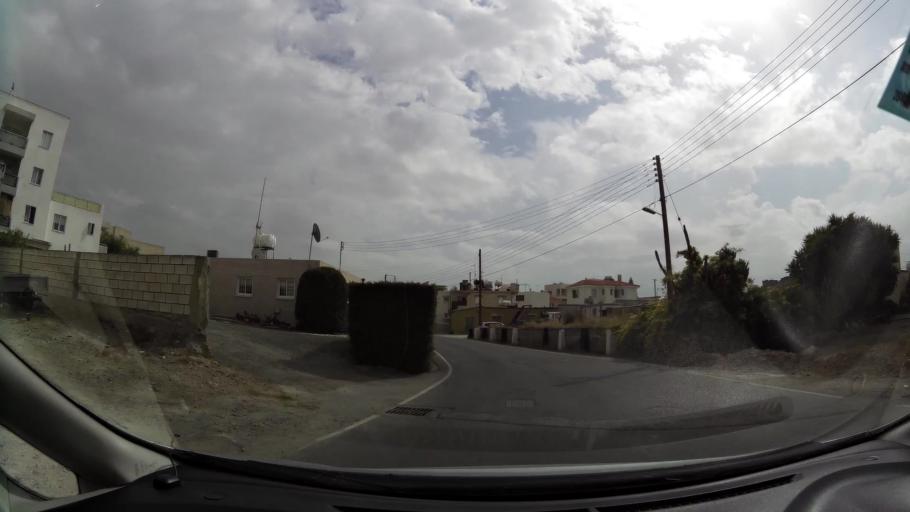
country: CY
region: Lefkosia
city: Geri
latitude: 35.1039
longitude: 33.3748
